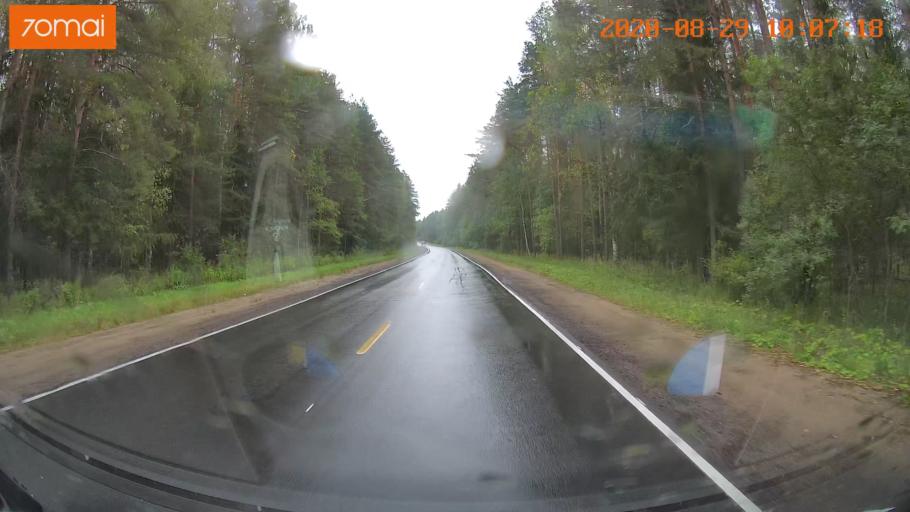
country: RU
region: Ivanovo
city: Kuznechikha
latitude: 57.3819
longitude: 42.5642
